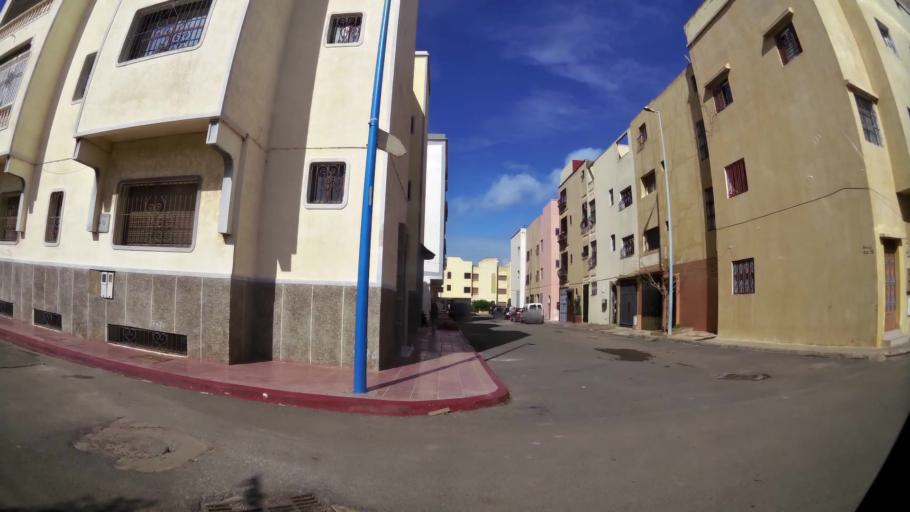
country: MA
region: Grand Casablanca
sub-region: Casablanca
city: Casablanca
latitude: 33.5652
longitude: -7.6974
